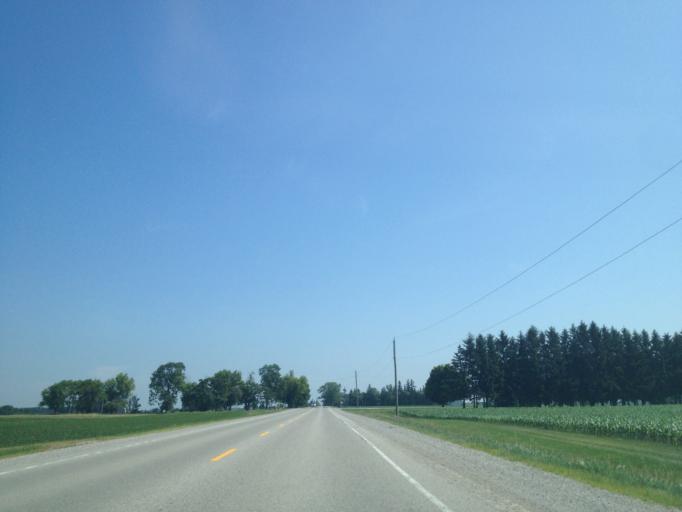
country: CA
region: Ontario
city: London
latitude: 43.2321
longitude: -81.2271
